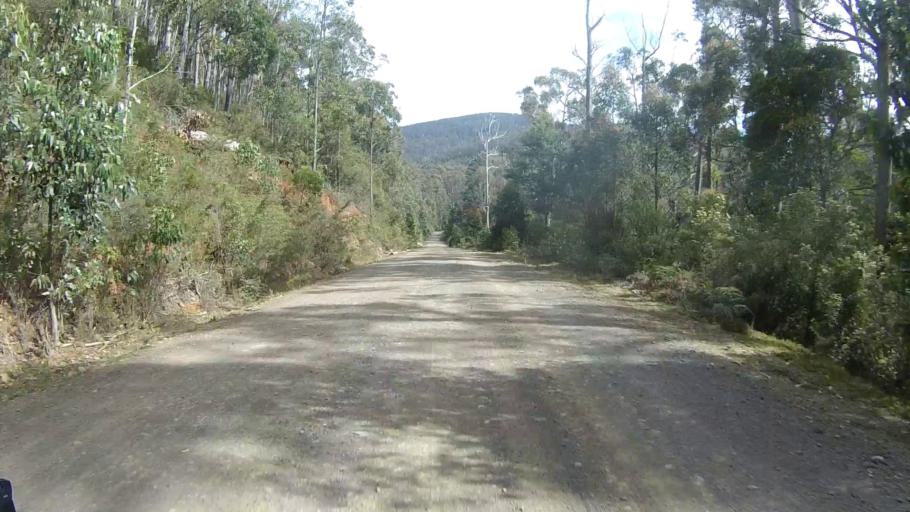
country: AU
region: Tasmania
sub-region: Sorell
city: Sorell
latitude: -42.7369
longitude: 147.8341
